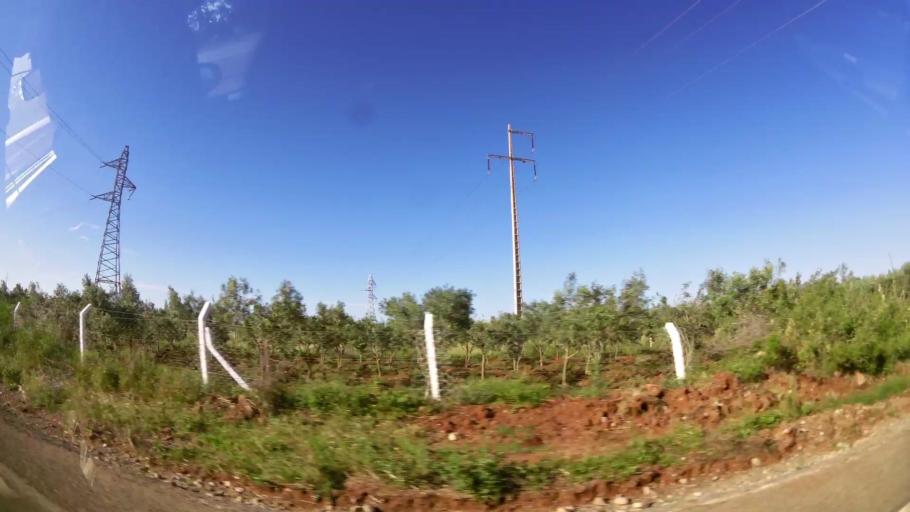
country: MA
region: Oriental
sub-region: Berkane-Taourirt
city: Ahfir
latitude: 34.9908
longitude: -2.1568
